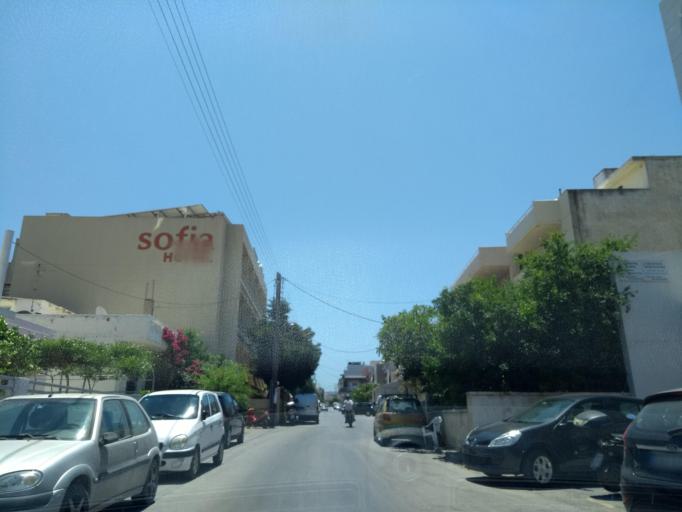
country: GR
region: Crete
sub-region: Nomos Irakleiou
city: Nea Alikarnassos
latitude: 35.3366
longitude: 25.1606
